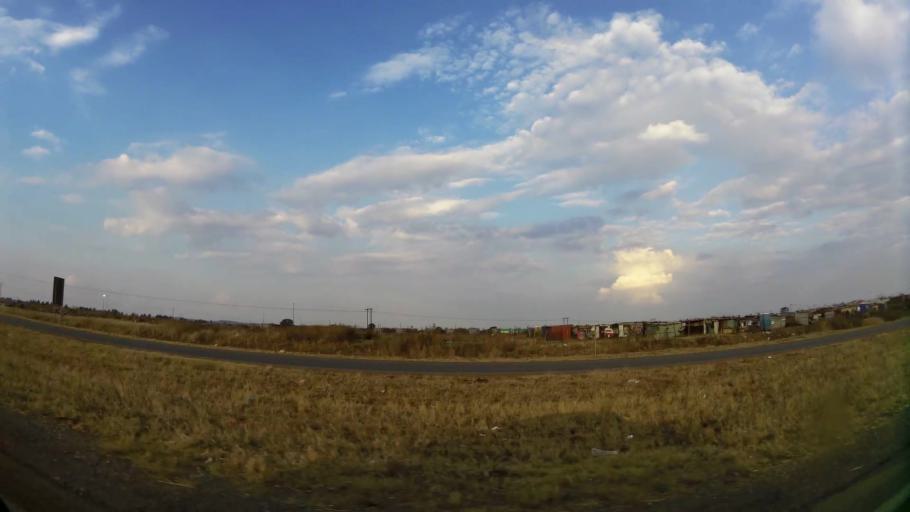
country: ZA
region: Gauteng
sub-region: Sedibeng District Municipality
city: Vanderbijlpark
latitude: -26.5980
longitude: 27.8194
